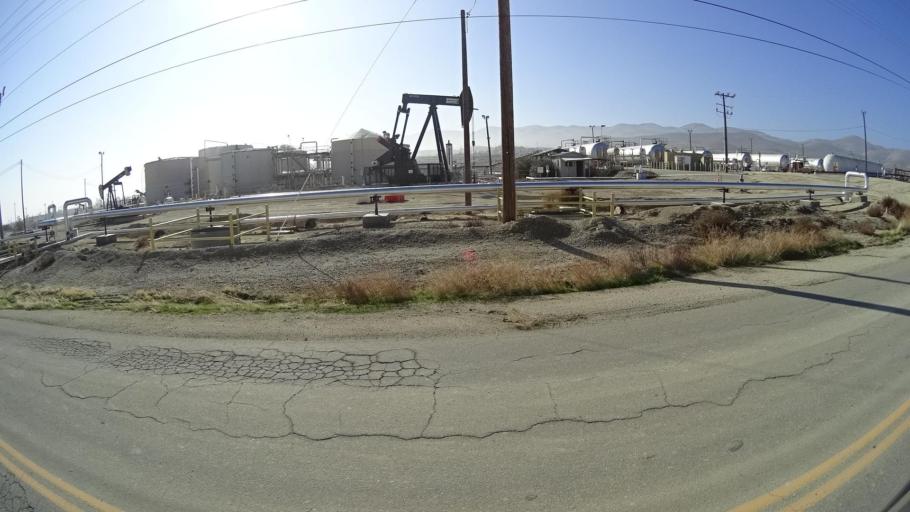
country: US
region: California
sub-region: Kern County
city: Taft Heights
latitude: 35.2228
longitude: -119.6175
